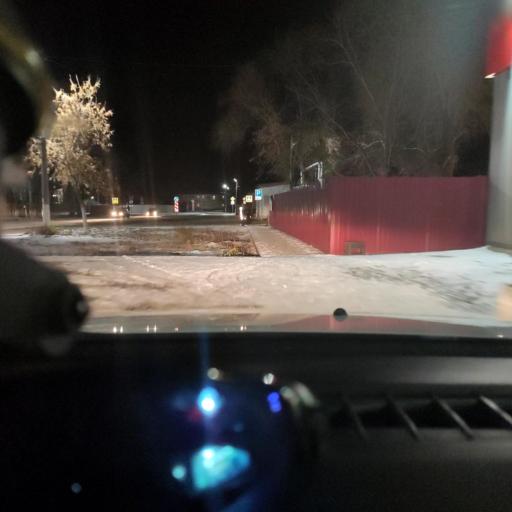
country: RU
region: Samara
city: Samara
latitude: 53.0825
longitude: 50.0922
